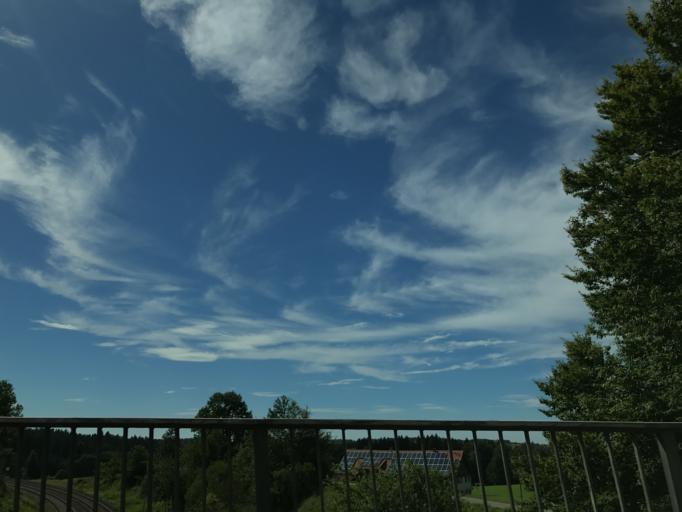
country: DE
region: Bavaria
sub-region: Swabia
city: Rothenbach
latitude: 47.6271
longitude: 9.9495
